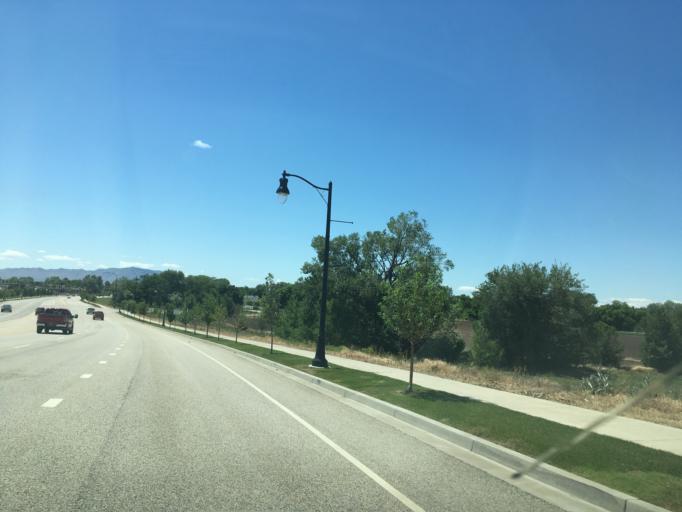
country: US
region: Utah
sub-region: Davis County
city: Layton
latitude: 41.0555
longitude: -111.9652
